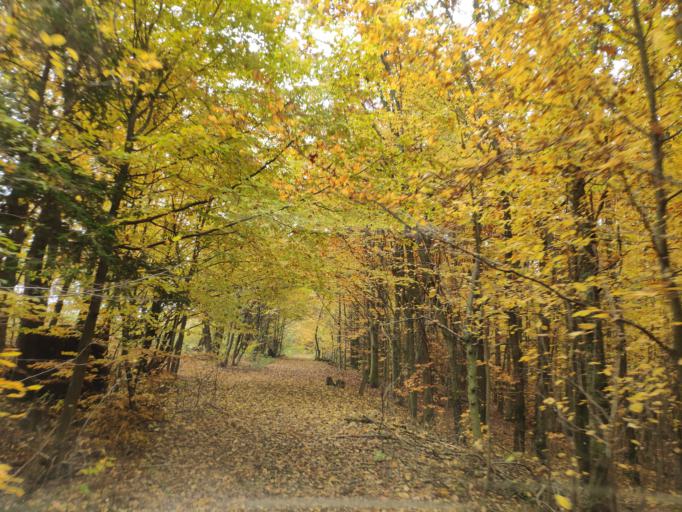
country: SK
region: Kosicky
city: Moldava nad Bodvou
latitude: 48.7252
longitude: 21.0963
